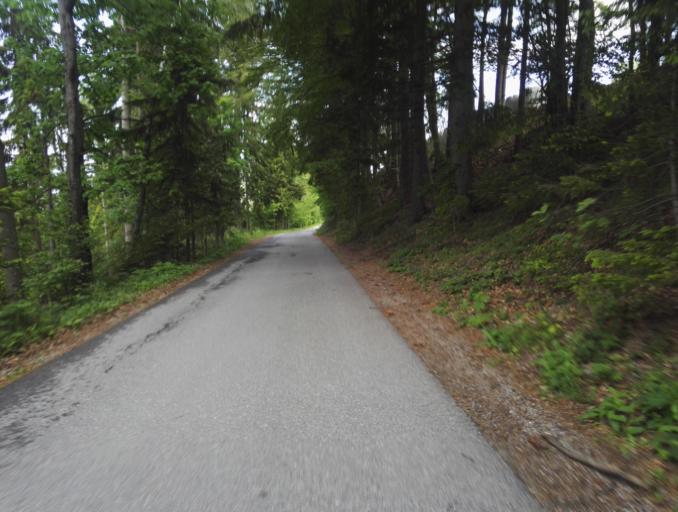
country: AT
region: Styria
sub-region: Politischer Bezirk Graz-Umgebung
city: Sankt Radegund bei Graz
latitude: 47.2074
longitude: 15.4583
